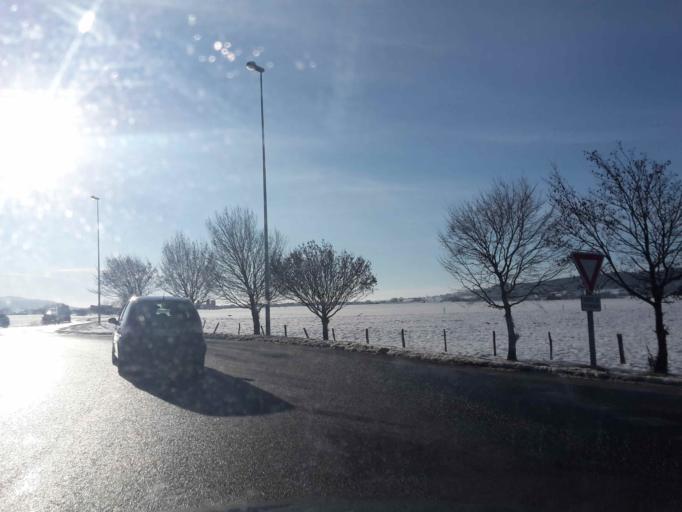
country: FR
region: Franche-Comte
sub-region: Departement du Doubs
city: Doubs
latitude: 46.9249
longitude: 6.3373
